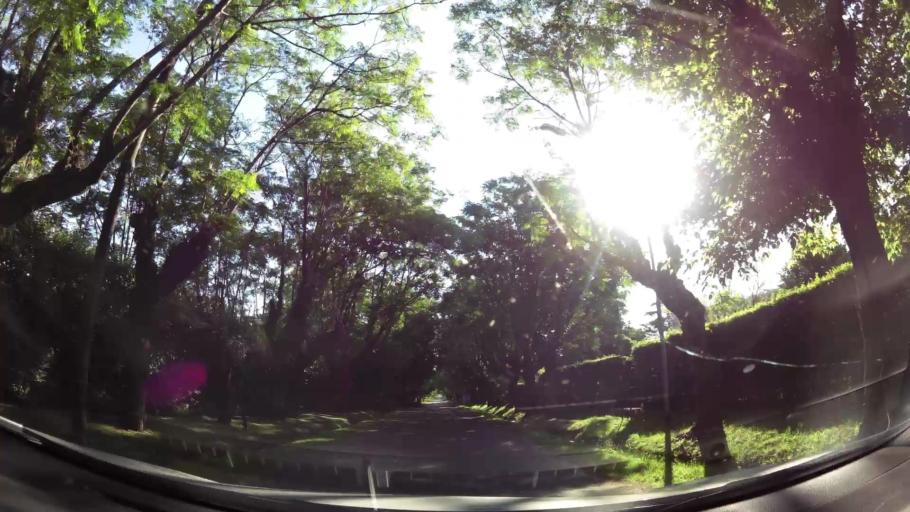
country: AR
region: Buenos Aires
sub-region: Partido de Tigre
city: Tigre
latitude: -34.4728
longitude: -58.6359
